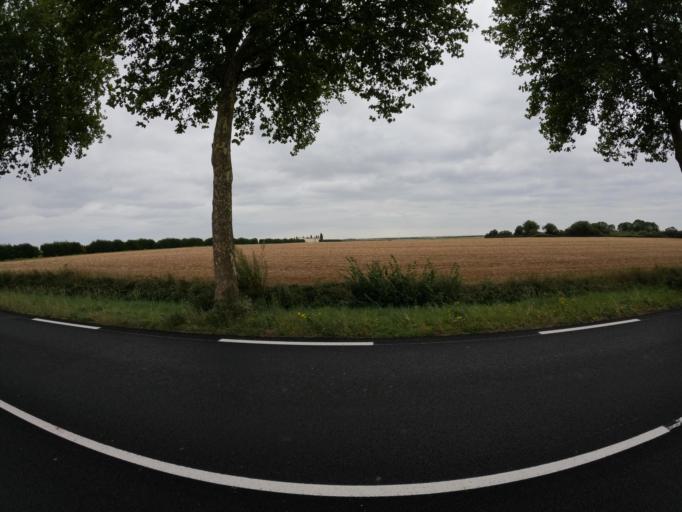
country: FR
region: Pays de la Loire
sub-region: Departement de la Vendee
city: Le Langon
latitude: 46.5030
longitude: -0.9384
